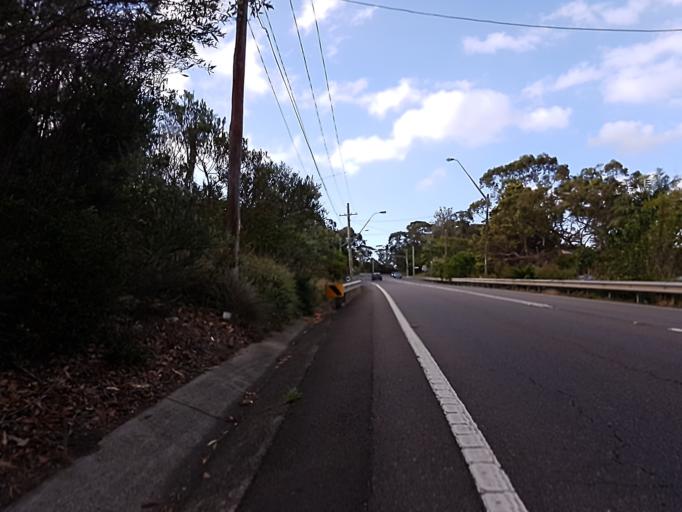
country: AU
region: New South Wales
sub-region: Warringah
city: Allambie Heights
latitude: -33.7839
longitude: 151.2387
